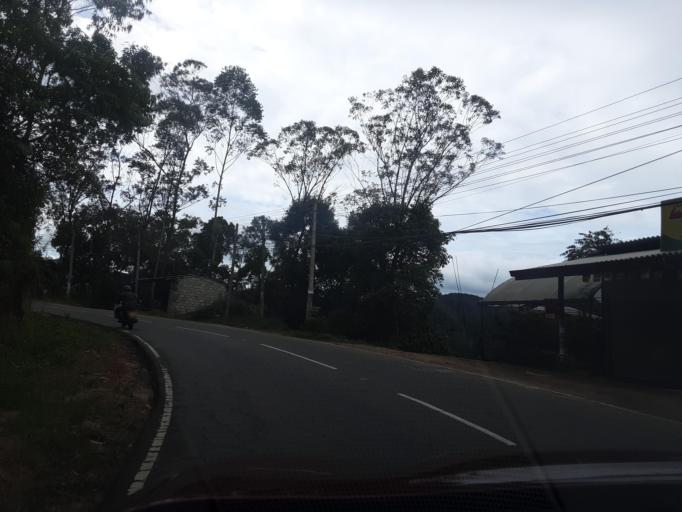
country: LK
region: Uva
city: Haputale
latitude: 6.8453
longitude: 80.9728
